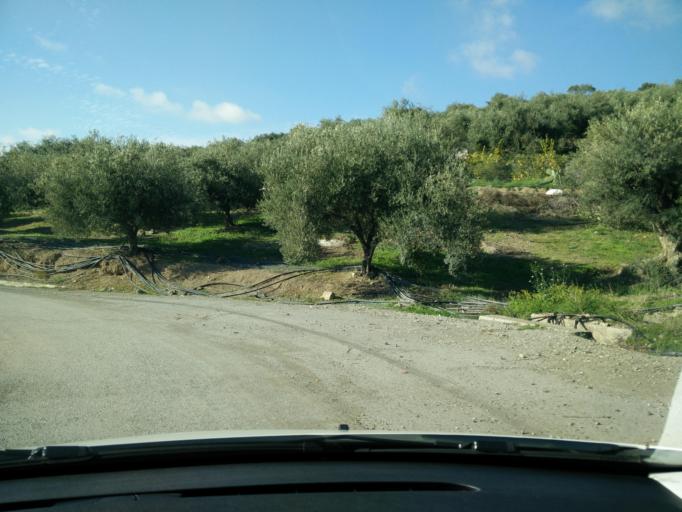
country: GR
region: Crete
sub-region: Nomos Lasithiou
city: Gra Liyia
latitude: 34.9993
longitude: 25.5186
